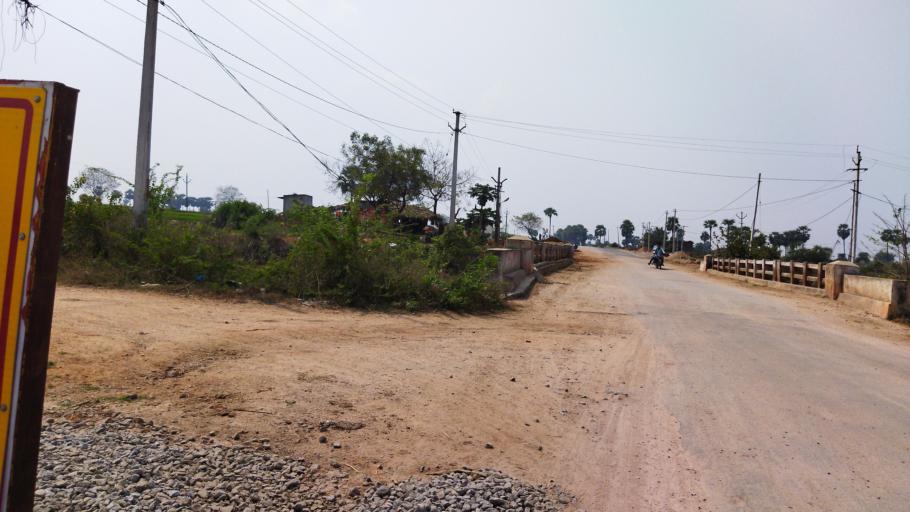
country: IN
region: Telangana
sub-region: Nalgonda
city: Nalgonda
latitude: 17.1113
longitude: 79.3581
